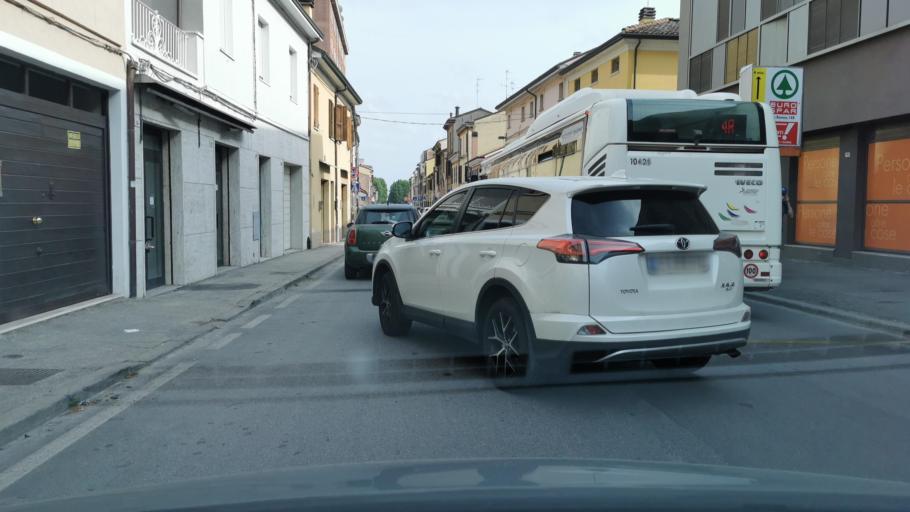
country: IT
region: Emilia-Romagna
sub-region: Provincia di Ravenna
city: Ravenna
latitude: 44.4114
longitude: 12.2067
